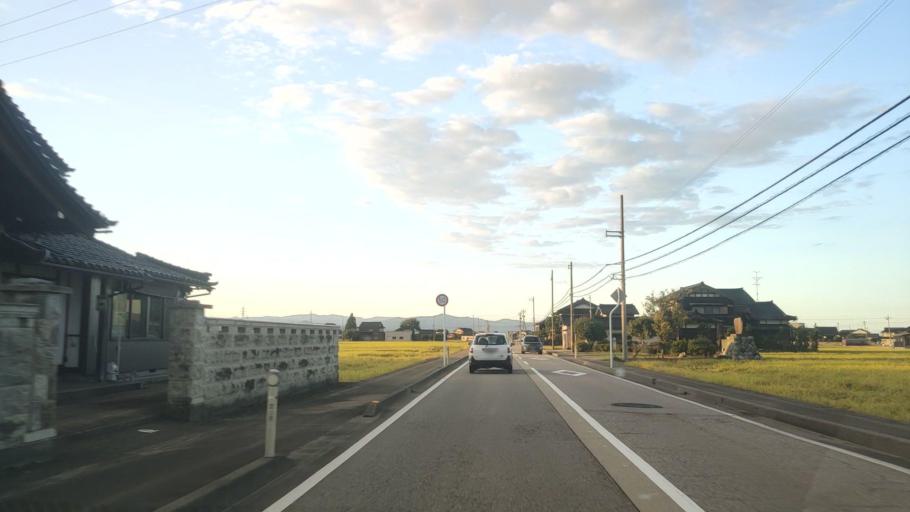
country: JP
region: Toyama
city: Nanto-shi
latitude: 36.6205
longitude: 136.8890
